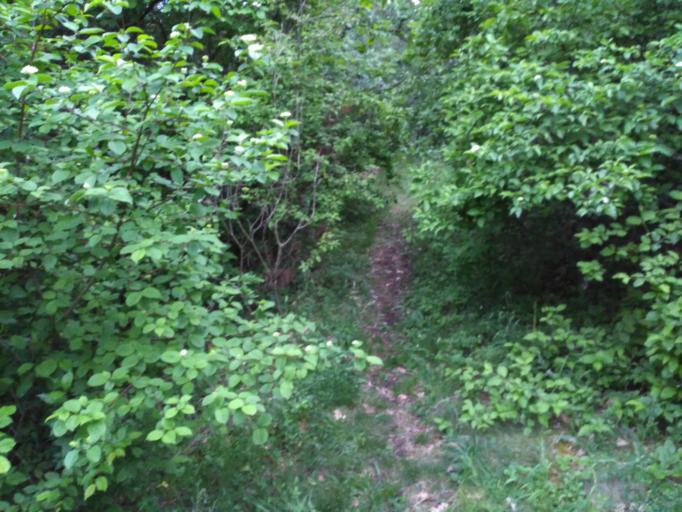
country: CZ
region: Central Bohemia
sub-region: Okres Beroun
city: Kraluv Dvur
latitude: 49.9201
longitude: 14.0231
